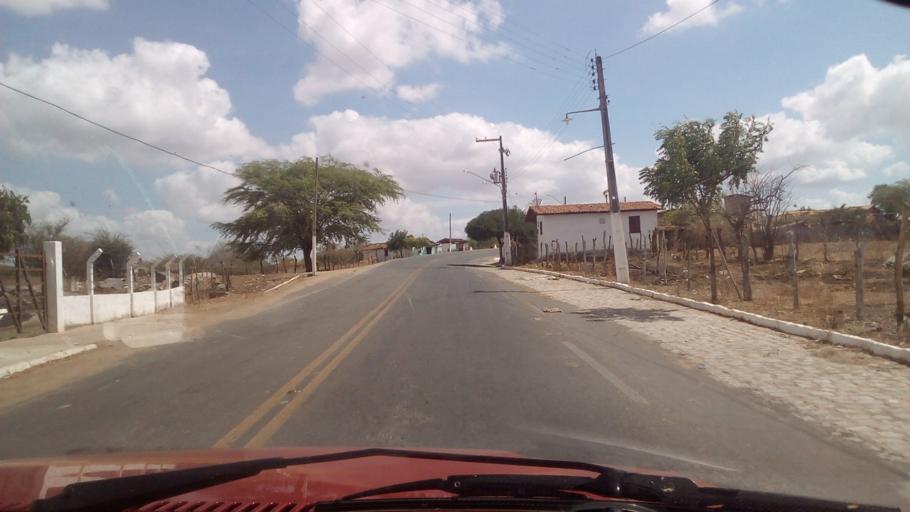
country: BR
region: Paraiba
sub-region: Dona Ines
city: Dona Ines
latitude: -6.5385
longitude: -35.6573
